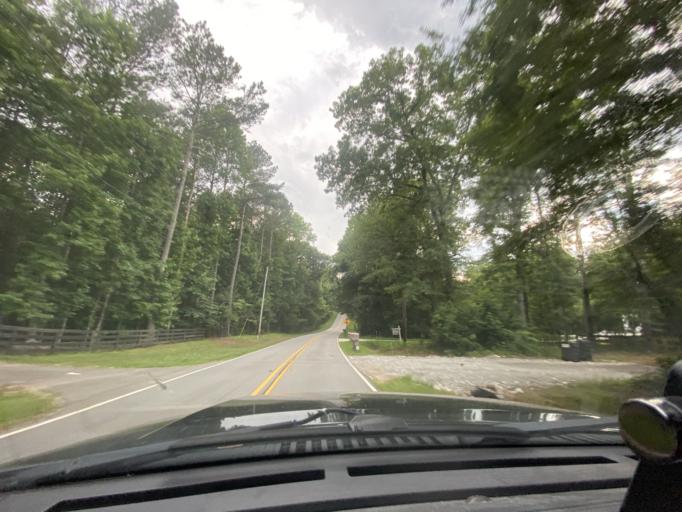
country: US
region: Georgia
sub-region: Fayette County
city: Peachtree City
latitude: 33.4205
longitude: -84.6799
